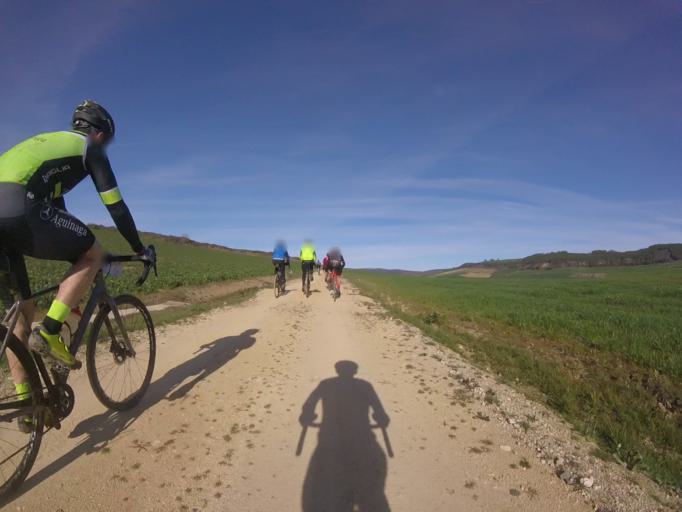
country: ES
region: Navarre
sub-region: Provincia de Navarra
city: Yerri
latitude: 42.7176
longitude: -1.9597
